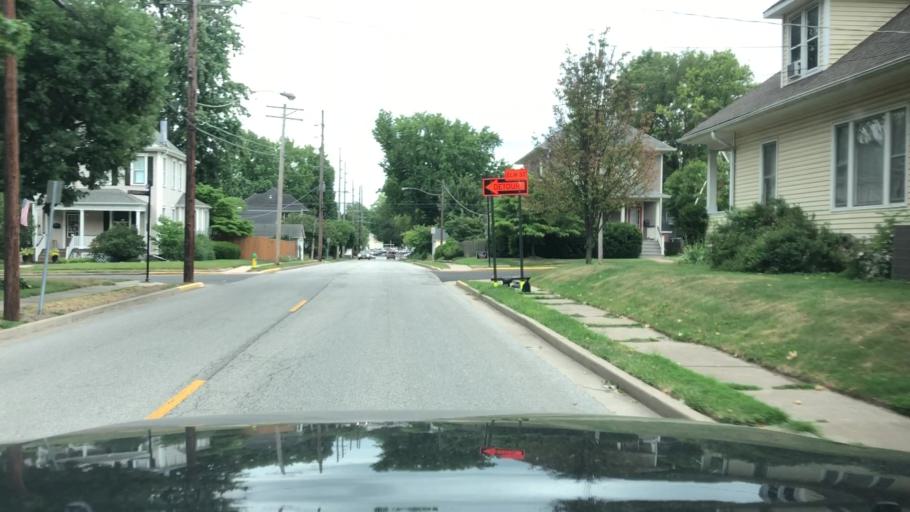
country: US
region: Missouri
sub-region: Saint Charles County
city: Saint Charles
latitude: 38.7885
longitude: -90.4960
